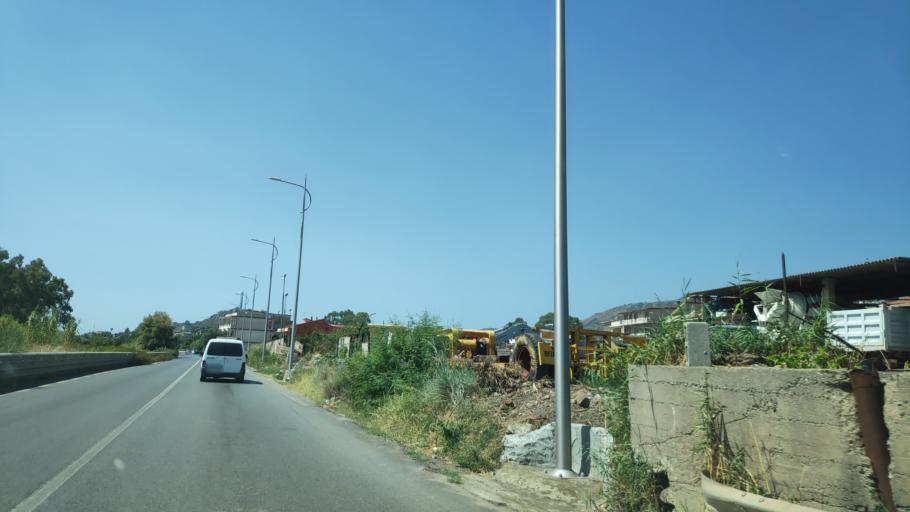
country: IT
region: Calabria
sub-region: Provincia di Reggio Calabria
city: Brancaleone-Marina
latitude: 37.9743
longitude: 16.1095
